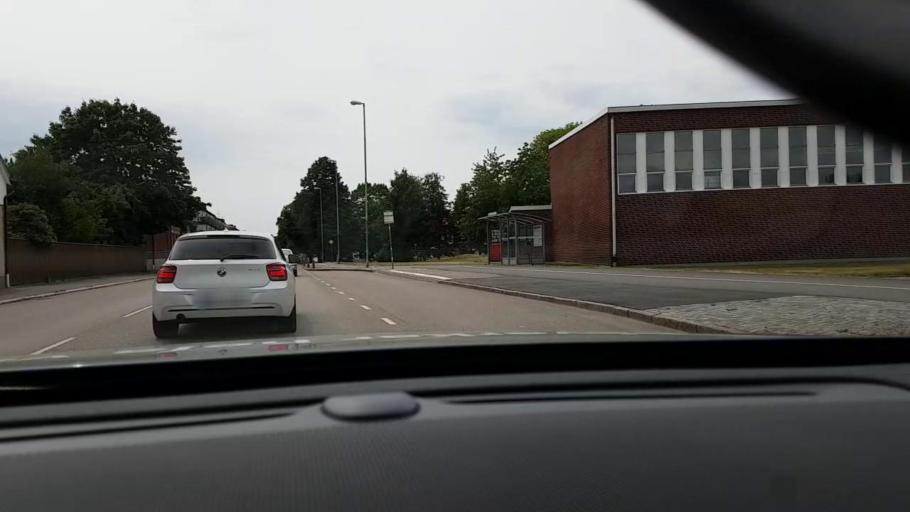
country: SE
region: Skane
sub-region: Hassleholms Kommun
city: Hassleholm
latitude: 56.1618
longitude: 13.7723
